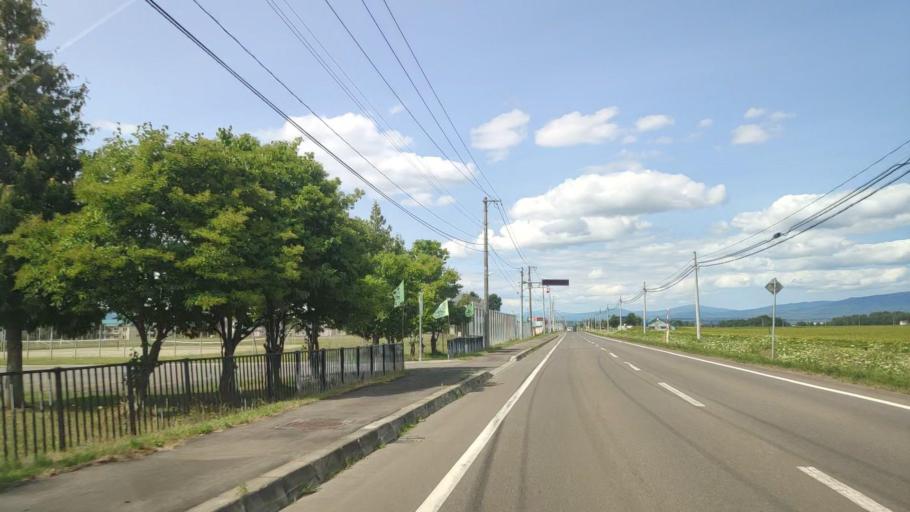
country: JP
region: Hokkaido
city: Nayoro
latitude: 44.2913
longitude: 142.4294
